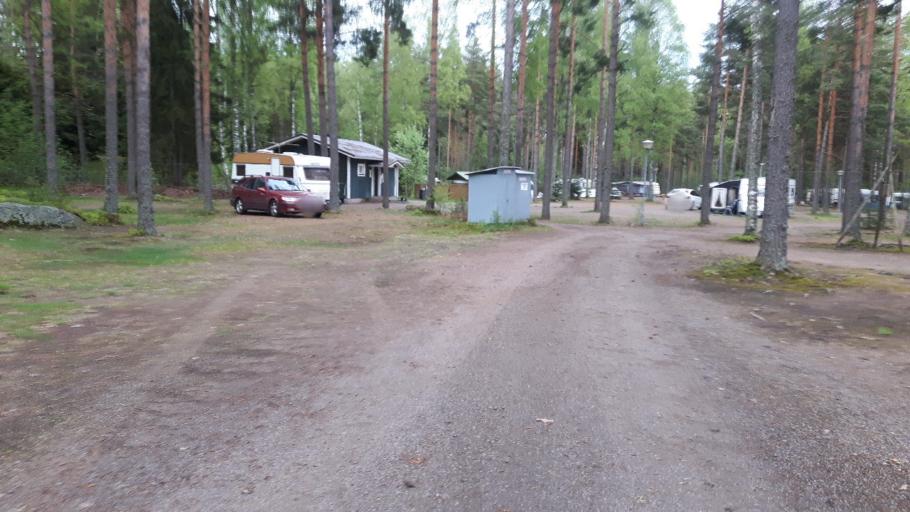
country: FI
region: Kymenlaakso
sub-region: Kotka-Hamina
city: Hamina
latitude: 60.5259
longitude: 27.2539
